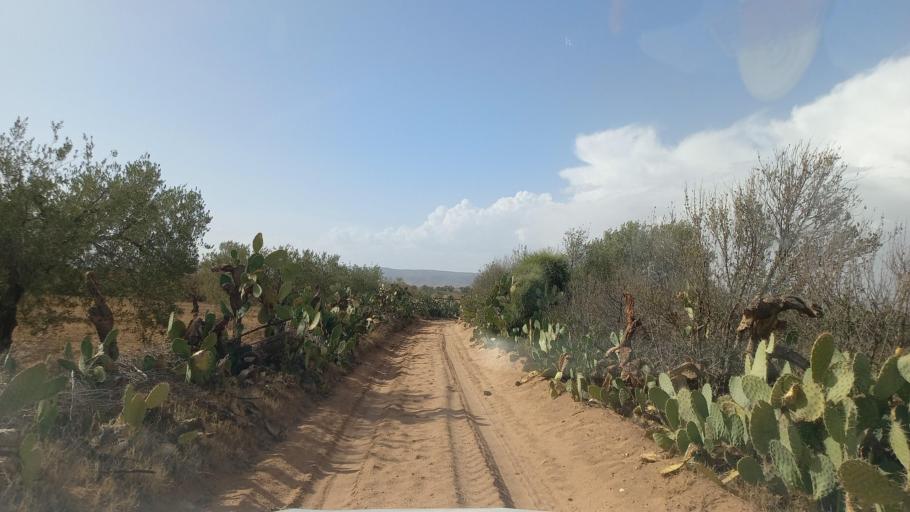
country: TN
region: Al Qasrayn
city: Kasserine
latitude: 35.2162
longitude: 8.9485
